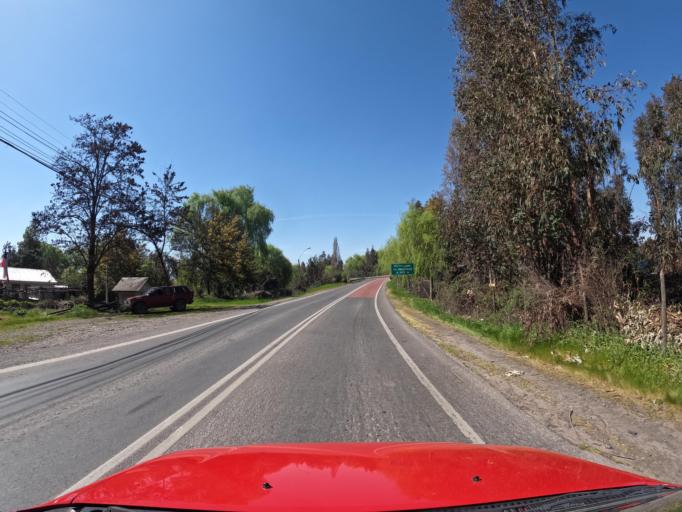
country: CL
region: Maule
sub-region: Provincia de Curico
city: Rauco
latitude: -34.9947
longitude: -71.3508
